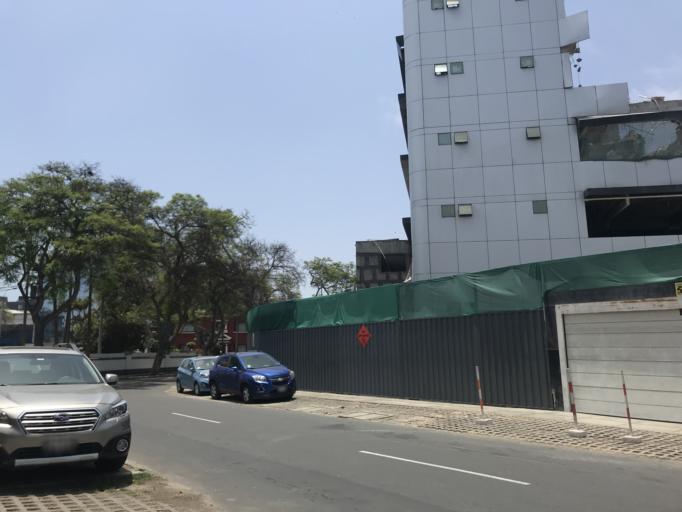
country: PE
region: Lima
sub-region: Lima
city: San Isidro
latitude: -12.1070
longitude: -77.0338
